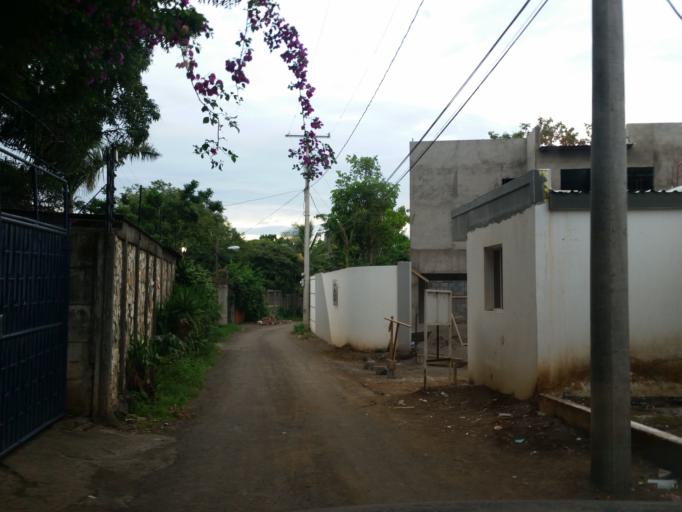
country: NI
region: Managua
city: Managua
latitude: 12.0903
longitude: -86.2373
